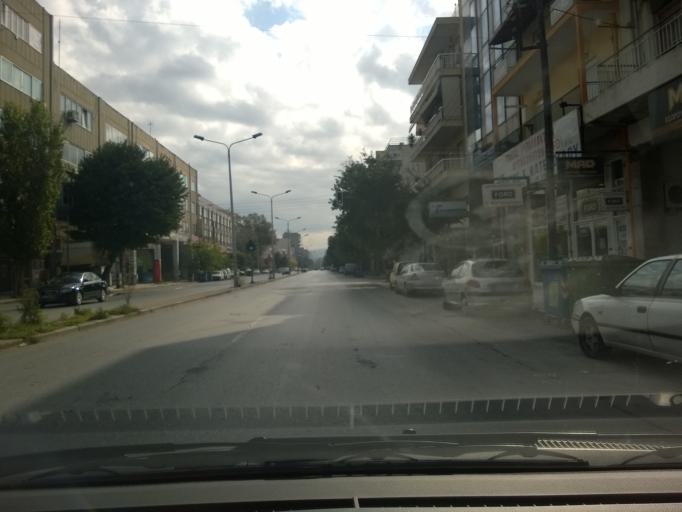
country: GR
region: Central Macedonia
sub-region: Nomos Thessalonikis
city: Ampelokipoi
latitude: 40.6497
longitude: 22.9173
